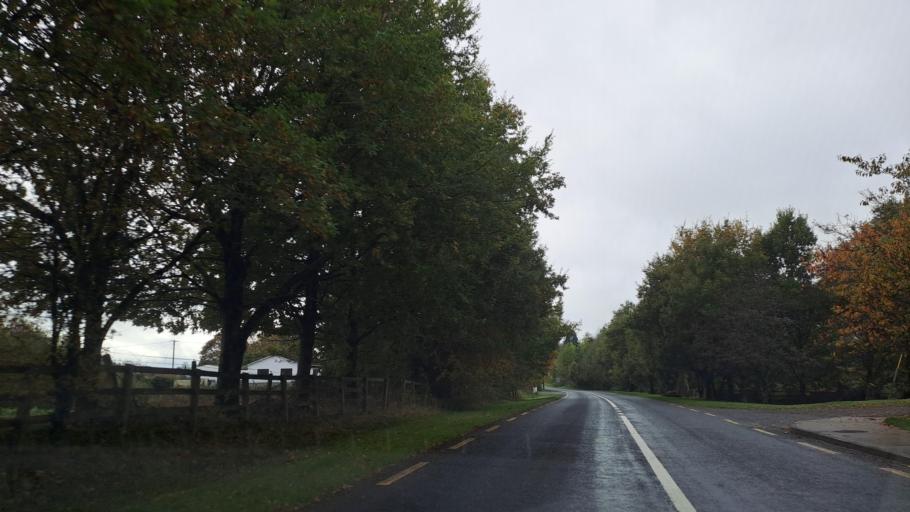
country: IE
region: Ulster
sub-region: An Cabhan
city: Bailieborough
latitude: 53.9090
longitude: -6.9770
